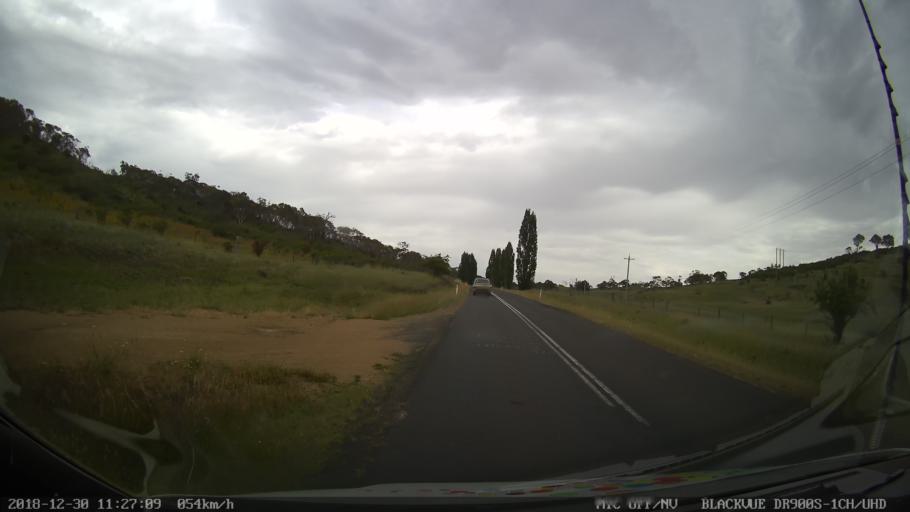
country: AU
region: New South Wales
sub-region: Snowy River
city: Jindabyne
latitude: -36.4629
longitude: 148.6287
